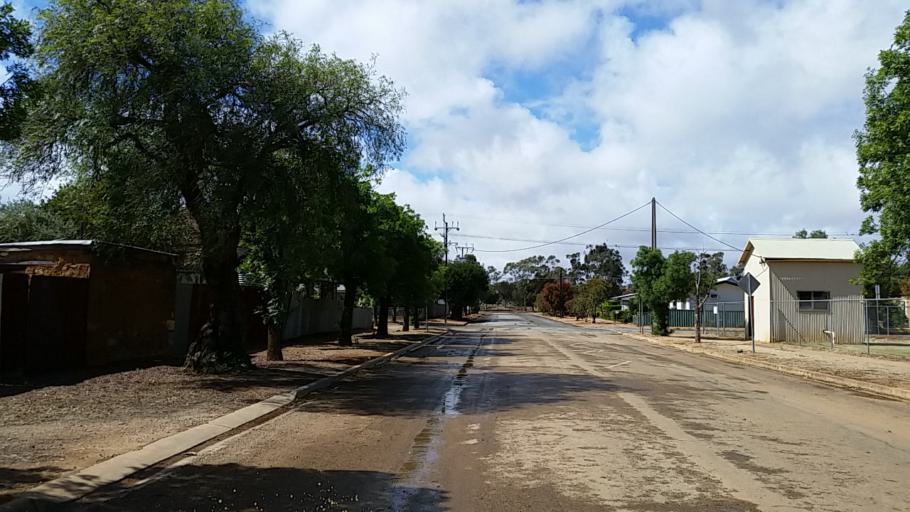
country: AU
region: South Australia
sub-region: Peterborough
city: Peterborough
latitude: -32.9721
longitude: 138.8332
